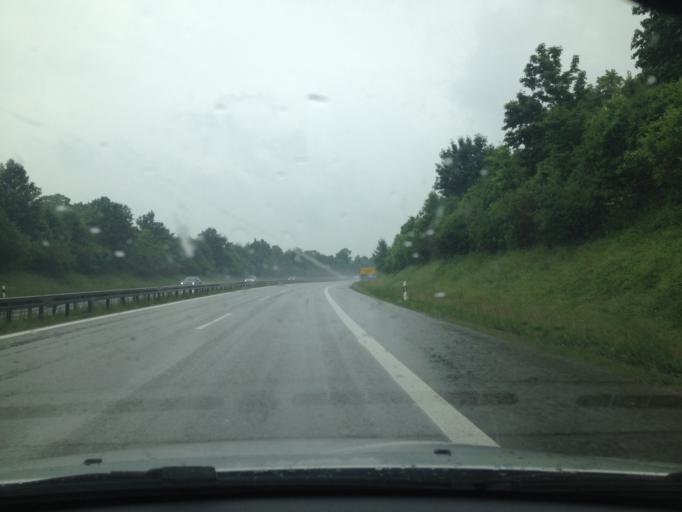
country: DE
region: Bavaria
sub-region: Swabia
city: Klosterlechfeld
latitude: 48.1613
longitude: 10.8378
